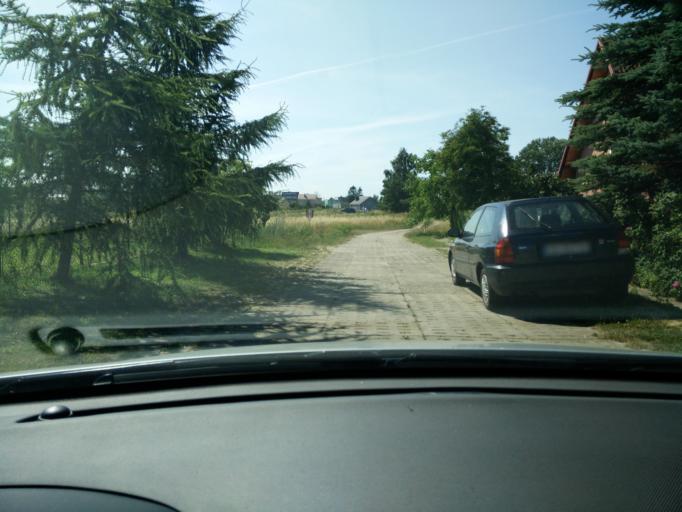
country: PL
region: Pomeranian Voivodeship
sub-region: Powiat pucki
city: Mosty
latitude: 54.6299
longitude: 18.5027
